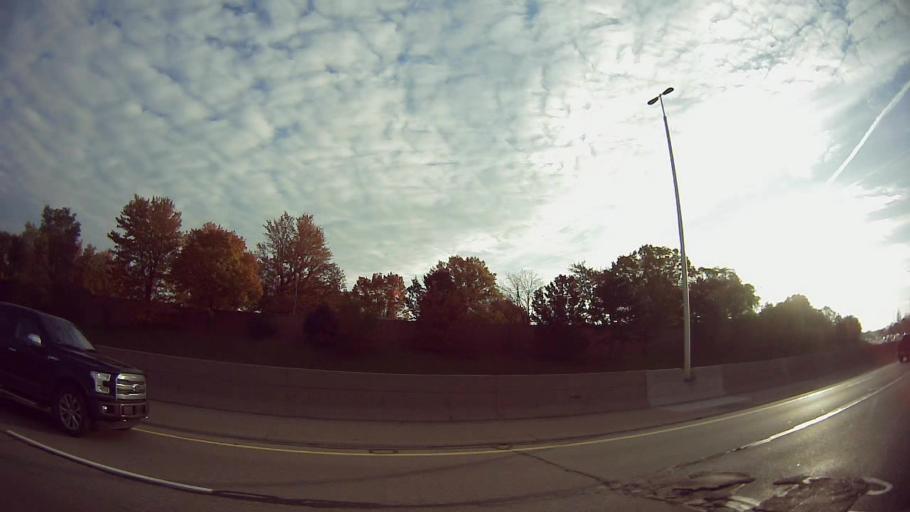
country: US
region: Michigan
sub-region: Wayne County
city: Grosse Pointe Woods
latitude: 42.4556
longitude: -82.9238
